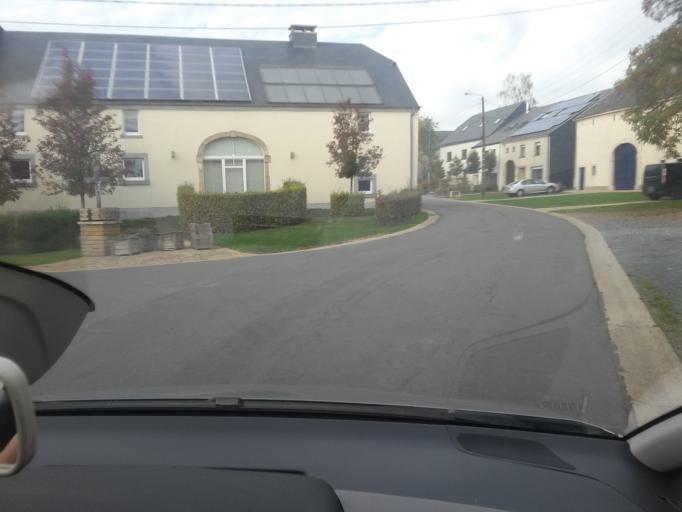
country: BE
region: Wallonia
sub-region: Province du Luxembourg
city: Attert
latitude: 49.7074
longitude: 5.7250
